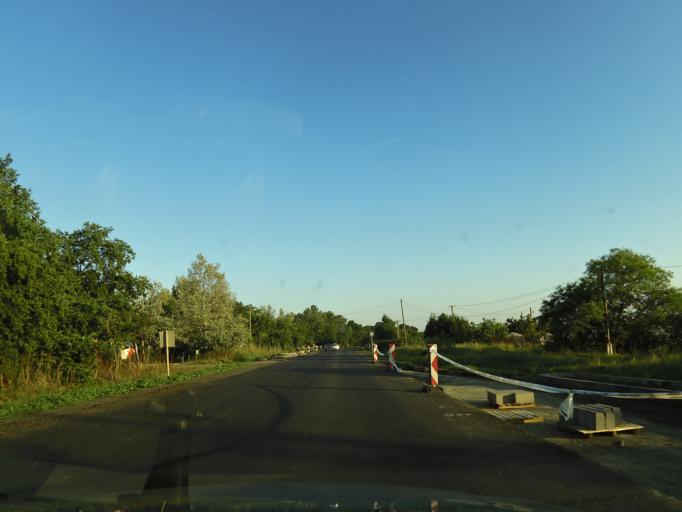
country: HU
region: Csongrad
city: Szentes
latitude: 46.6049
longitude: 20.2928
